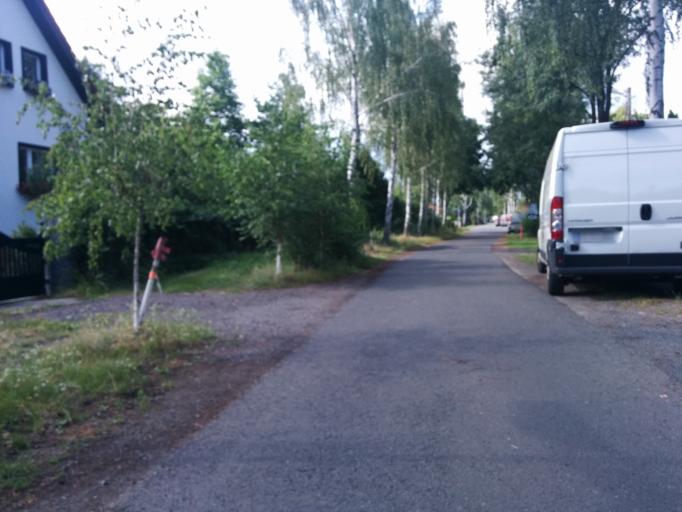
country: DE
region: Berlin
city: Biesdorf
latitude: 52.4844
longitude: 13.5703
